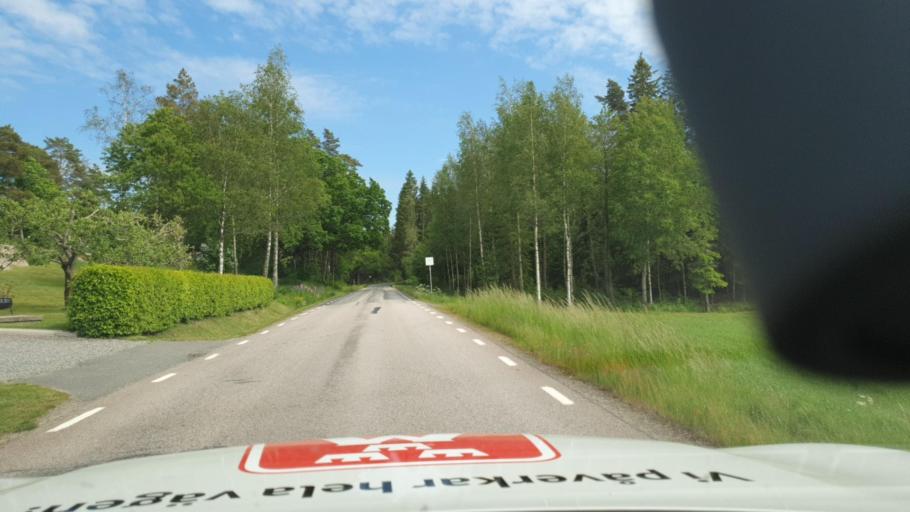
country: SE
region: Vaestra Goetaland
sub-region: Alingsas Kommun
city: Sollebrunn
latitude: 58.2121
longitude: 12.5387
